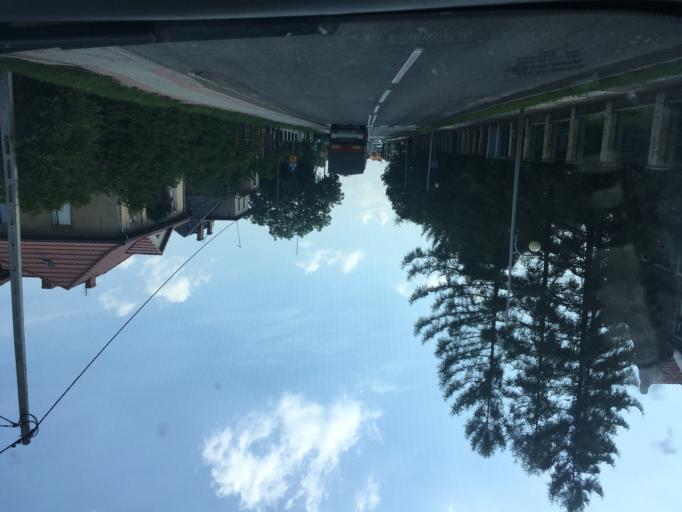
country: PL
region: Opole Voivodeship
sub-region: Powiat glubczycki
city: Glubczyce
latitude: 50.1950
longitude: 17.8391
